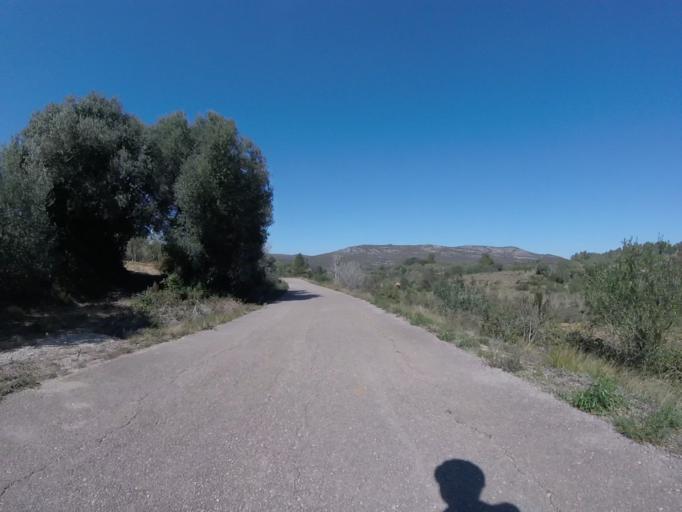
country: ES
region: Valencia
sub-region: Provincia de Castello
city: Cuevas de Vinroma
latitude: 40.3833
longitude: 0.1512
